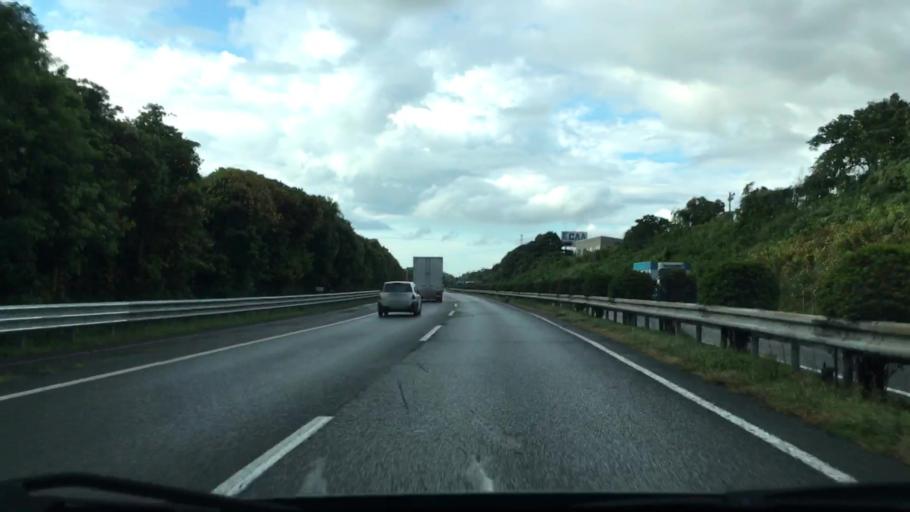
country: JP
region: Fukuoka
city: Koga
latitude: 33.6985
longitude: 130.4854
